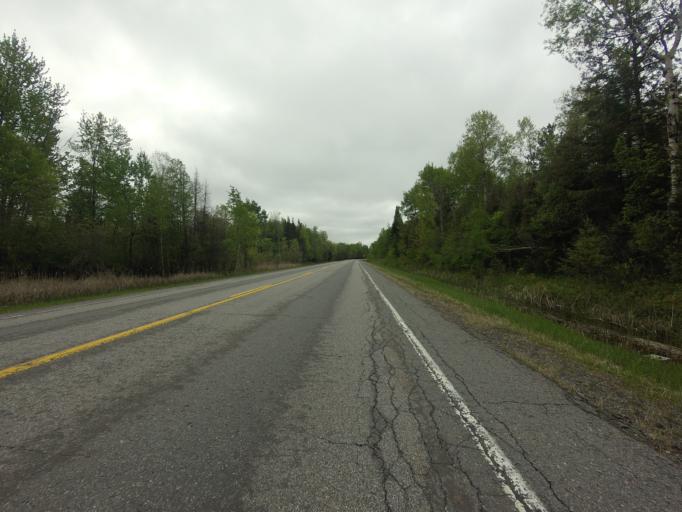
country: US
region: New York
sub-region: St. Lawrence County
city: Norfolk
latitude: 44.9961
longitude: -75.1589
